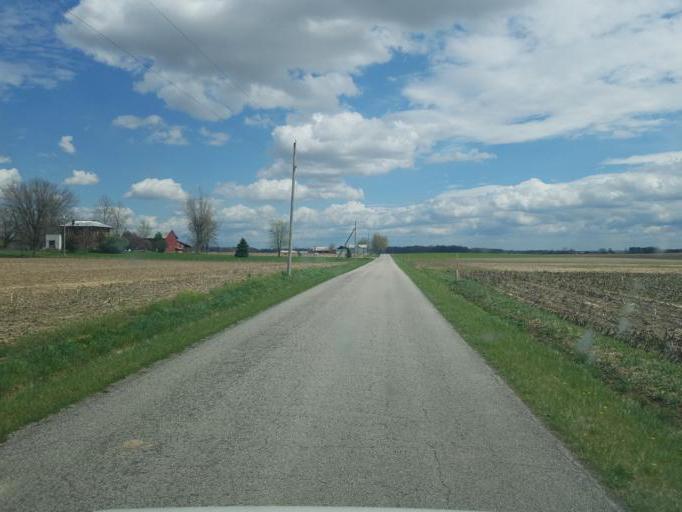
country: US
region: Ohio
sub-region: Crawford County
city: Bucyrus
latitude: 40.9067
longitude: -82.9392
